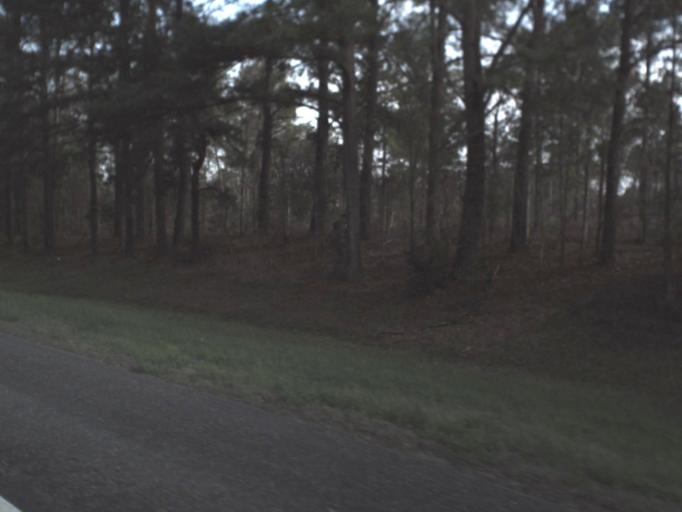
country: US
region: Florida
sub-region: Leon County
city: Tallahassee
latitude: 30.4781
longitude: -84.1106
